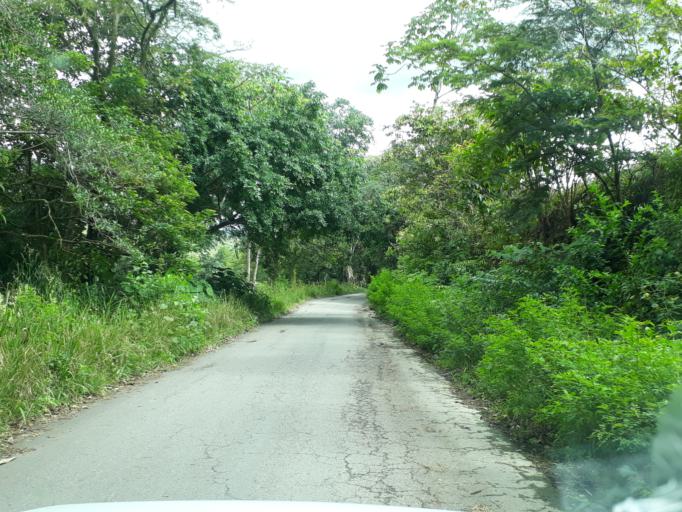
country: CO
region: Cundinamarca
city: Medina
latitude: 4.5286
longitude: -73.3567
